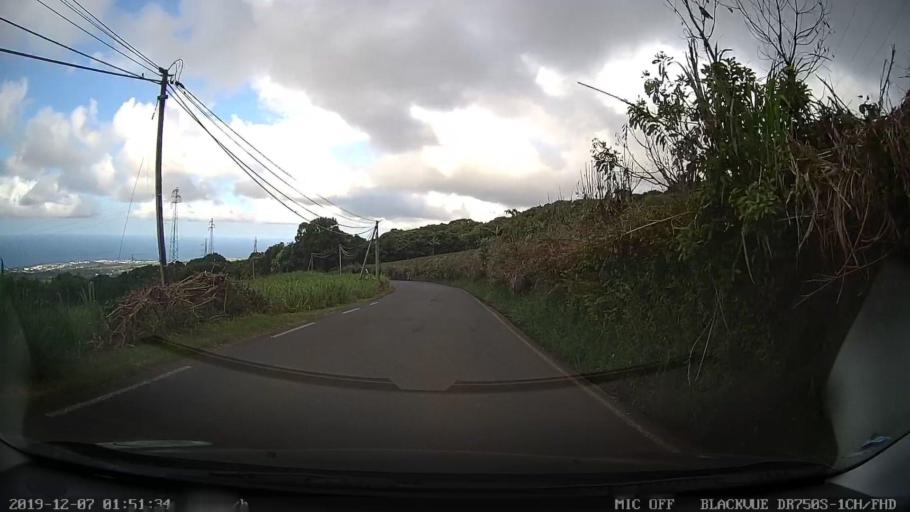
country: RE
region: Reunion
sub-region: Reunion
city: Sainte-Marie
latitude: -20.9426
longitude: 55.5343
